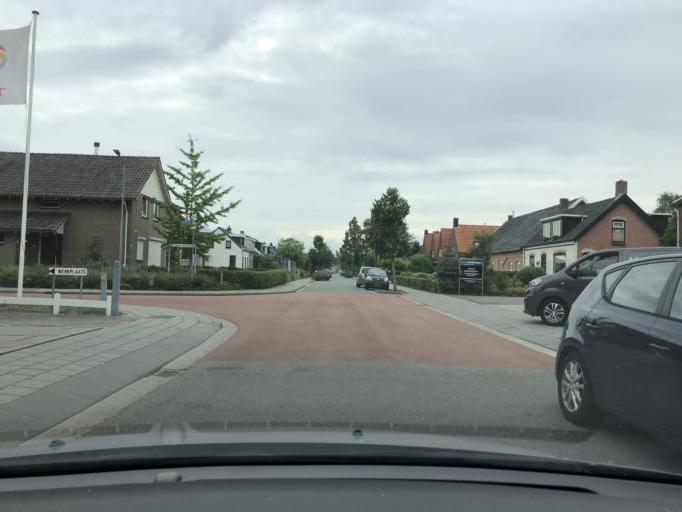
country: NL
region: Zeeland
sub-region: Gemeente Reimerswaal
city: Yerseke
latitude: 51.4283
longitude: 4.1177
